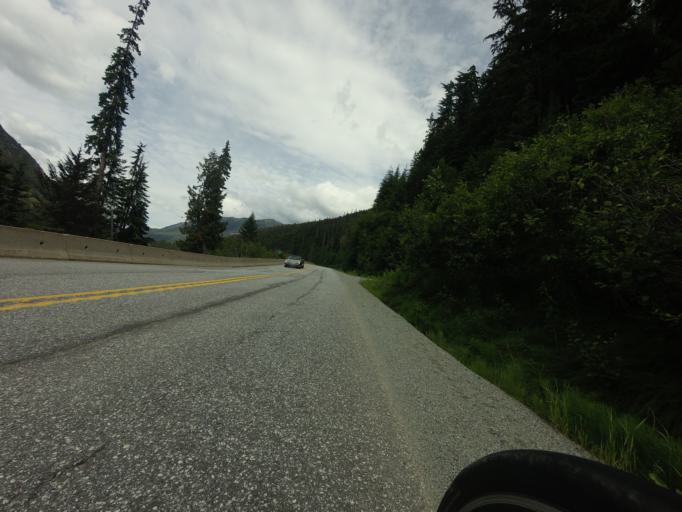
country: CA
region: British Columbia
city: Lillooet
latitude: 50.4126
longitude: -122.2869
